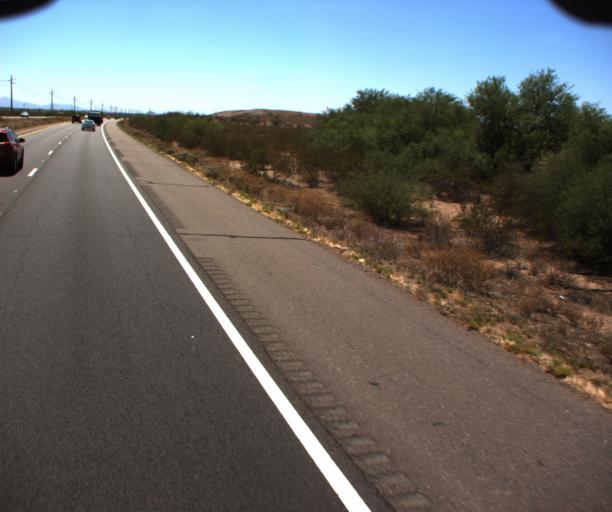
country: US
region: Arizona
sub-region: Maricopa County
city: Mesa
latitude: 33.5100
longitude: -111.7645
